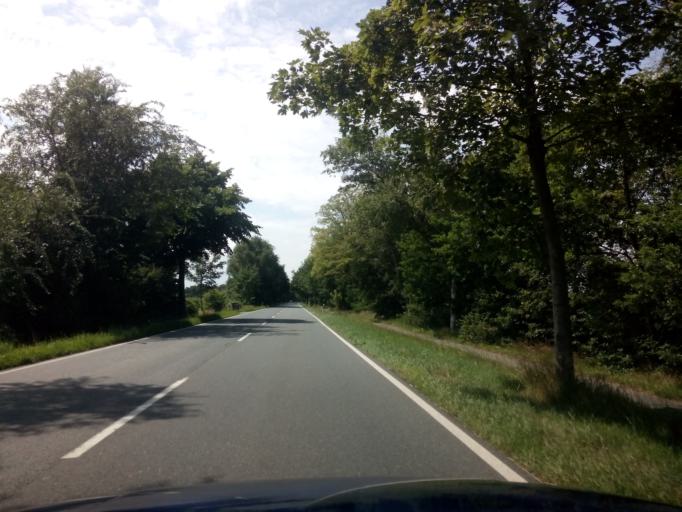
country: DE
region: Lower Saxony
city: Worpswede
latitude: 53.2567
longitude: 8.8886
